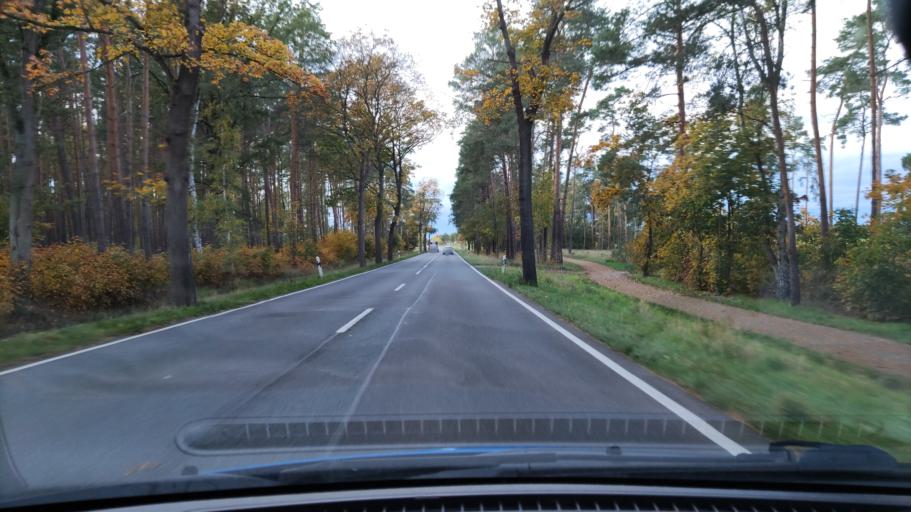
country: DE
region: Saxony-Anhalt
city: Luftkurort Arendsee
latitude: 52.8840
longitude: 11.5442
